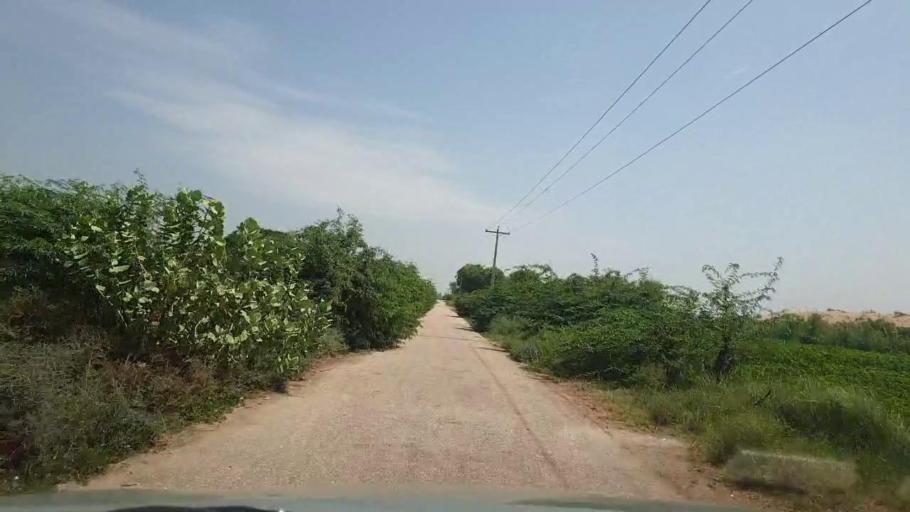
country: PK
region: Sindh
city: Bozdar
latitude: 27.1129
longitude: 68.9868
